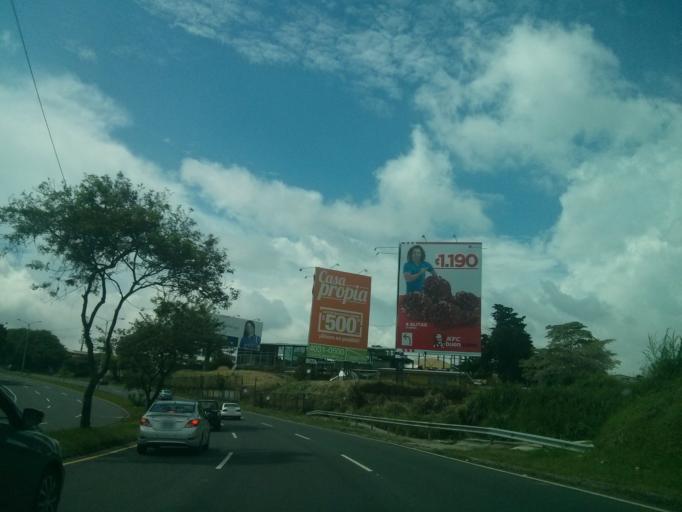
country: CR
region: San Jose
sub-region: Canton de Goicoechea
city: Guadalupe
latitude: 9.9415
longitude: -84.0565
